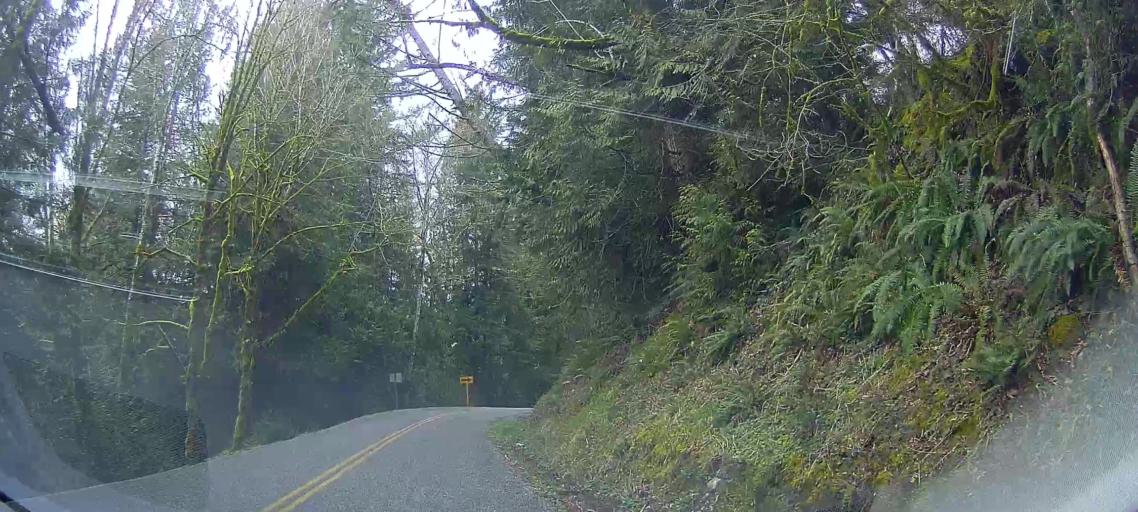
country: US
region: Washington
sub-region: Skagit County
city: Burlington
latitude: 48.5708
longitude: -122.3372
